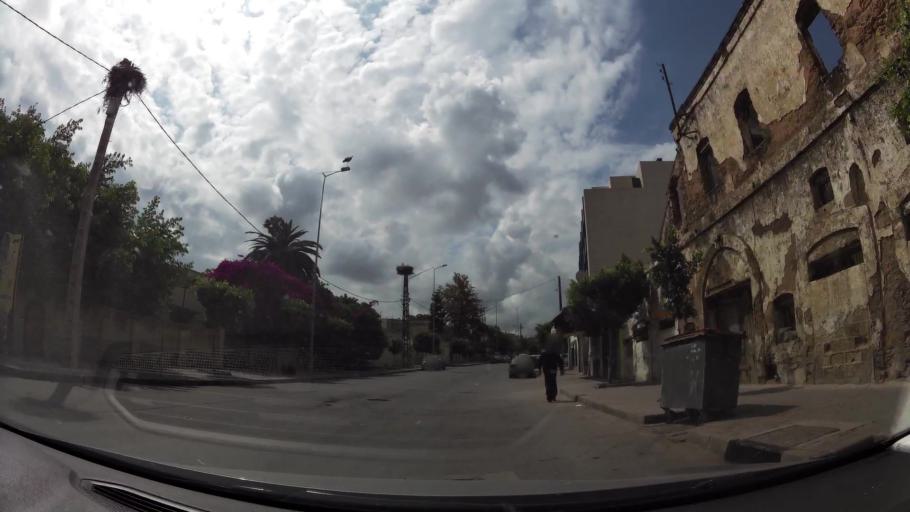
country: MA
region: Gharb-Chrarda-Beni Hssen
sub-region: Kenitra Province
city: Kenitra
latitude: 34.2658
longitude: -6.5711
